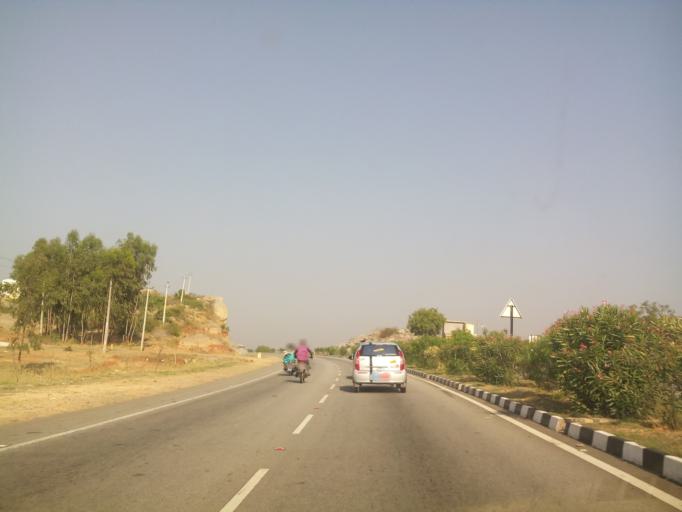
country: IN
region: Karnataka
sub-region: Bangalore Rural
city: Nelamangala
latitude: 13.0654
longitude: 77.2886
